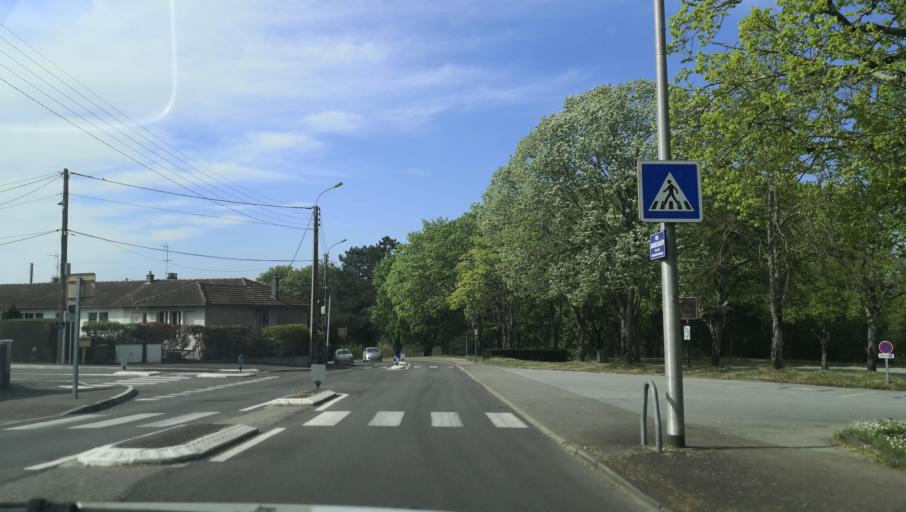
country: FR
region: Limousin
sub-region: Departement de la Haute-Vienne
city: Couzeix
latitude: 45.8583
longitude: 1.2581
